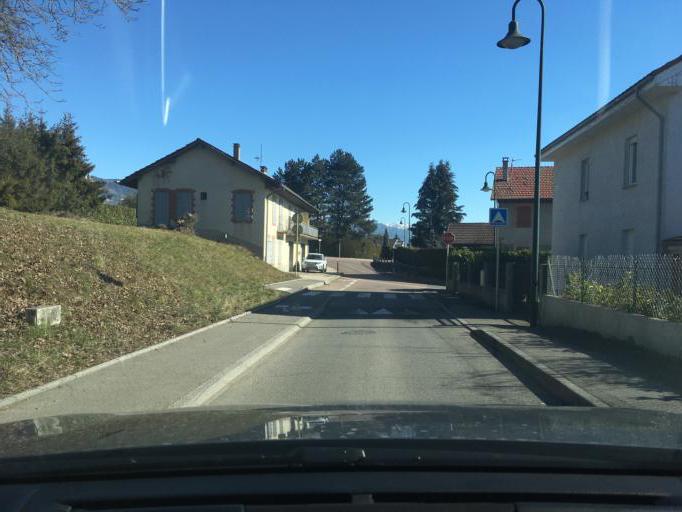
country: FR
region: Rhone-Alpes
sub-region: Departement de la Haute-Savoie
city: Vetraz-Monthoux
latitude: 46.1742
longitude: 6.2617
